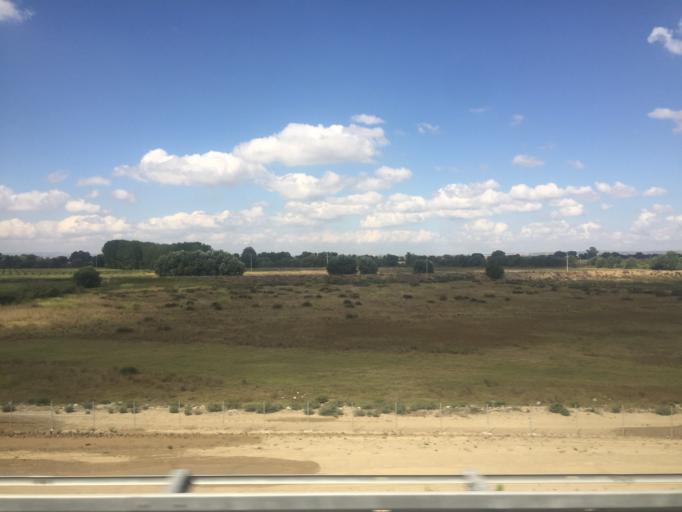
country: TR
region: Bursa
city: Tatkavakli
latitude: 40.1117
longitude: 28.2770
